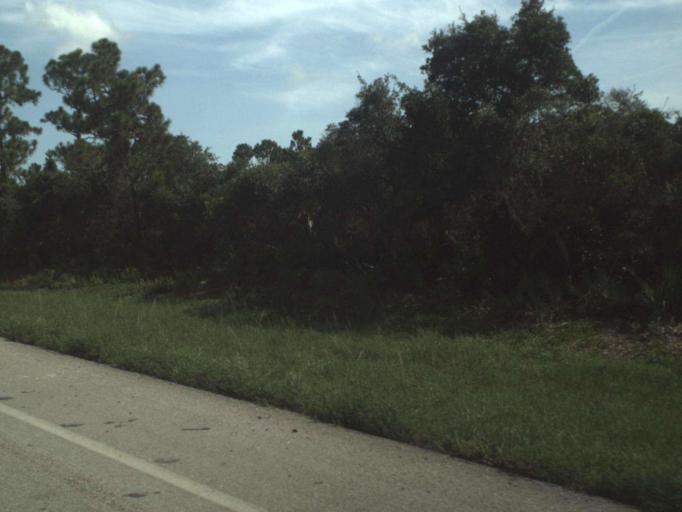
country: US
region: Florida
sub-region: Indian River County
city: West Vero Corridor
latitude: 27.6473
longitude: -80.5206
